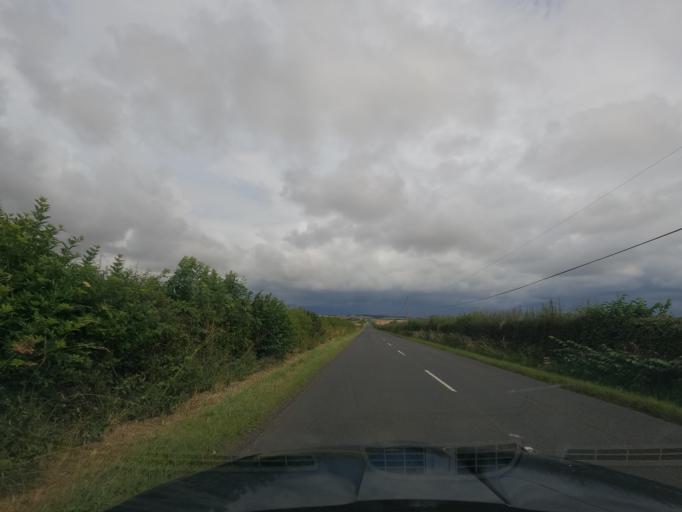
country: GB
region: England
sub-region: Northumberland
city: Ancroft
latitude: 55.6886
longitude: -2.0013
